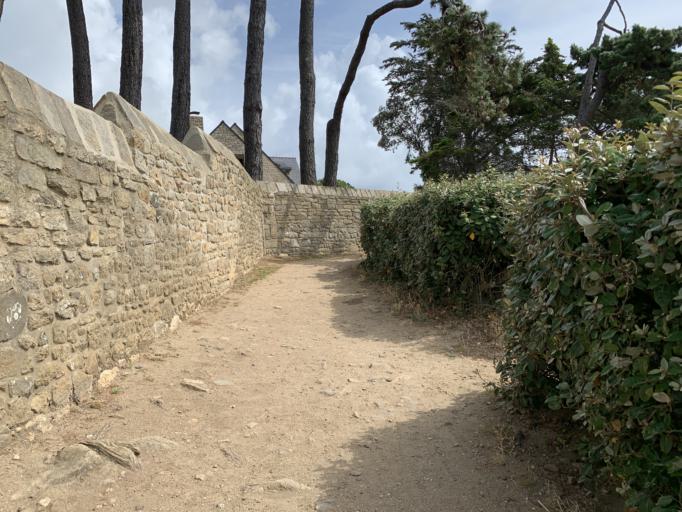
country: FR
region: Brittany
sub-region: Departement du Morbihan
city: Arradon
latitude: 47.6001
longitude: -2.8534
